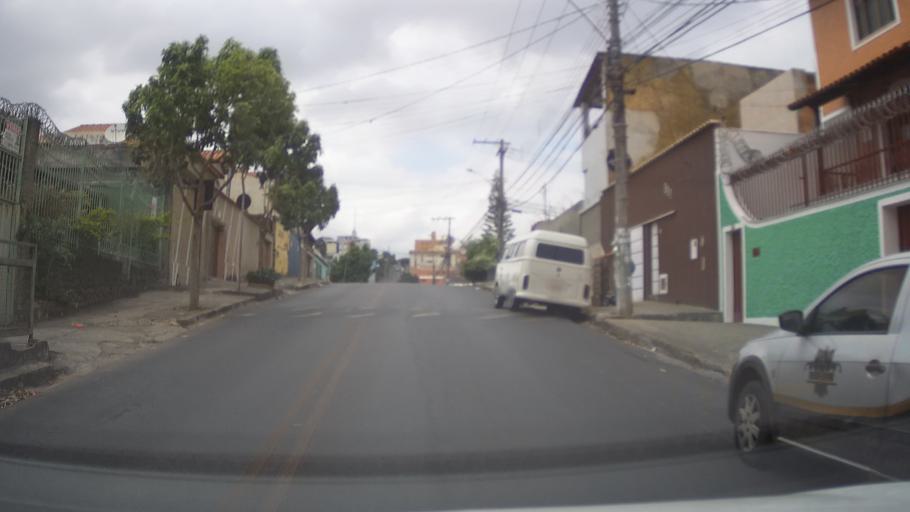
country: BR
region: Minas Gerais
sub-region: Belo Horizonte
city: Belo Horizonte
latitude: -19.9010
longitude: -43.9430
